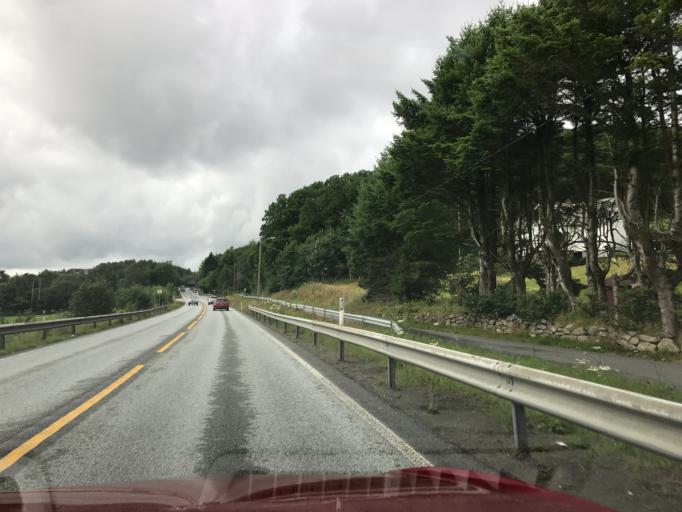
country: NO
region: Rogaland
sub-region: Tysvaer
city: Aksdal
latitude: 59.4229
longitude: 5.4231
